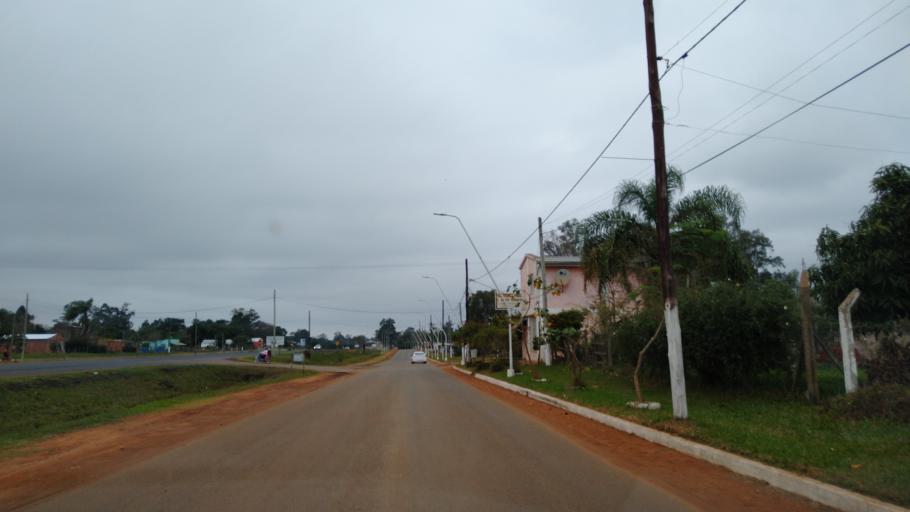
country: AR
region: Corrientes
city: Alvear
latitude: -29.0863
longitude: -56.5571
